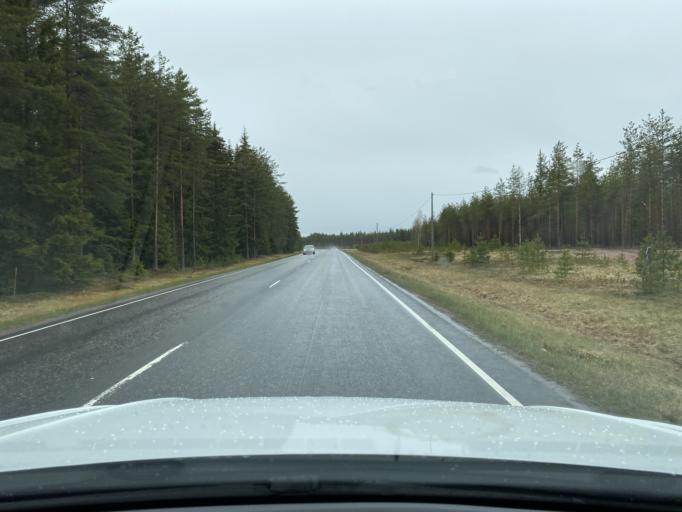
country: FI
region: Satakunta
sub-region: Pori
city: Vampula
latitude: 60.9535
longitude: 22.6694
